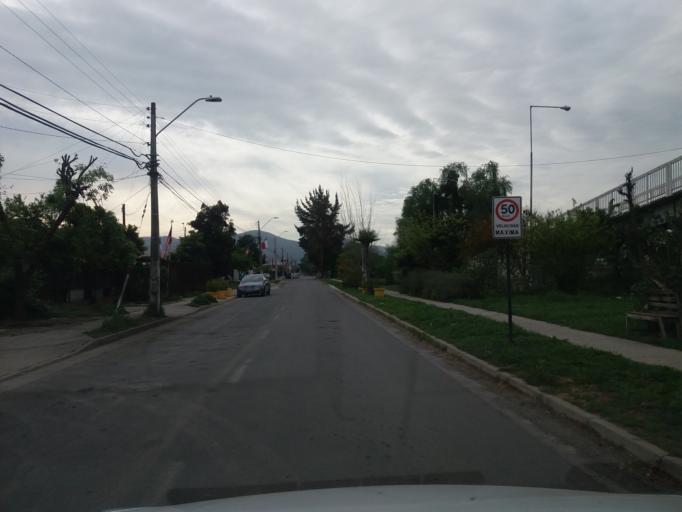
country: CL
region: Valparaiso
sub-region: Provincia de Quillota
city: Hacienda La Calera
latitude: -32.7862
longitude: -71.1712
